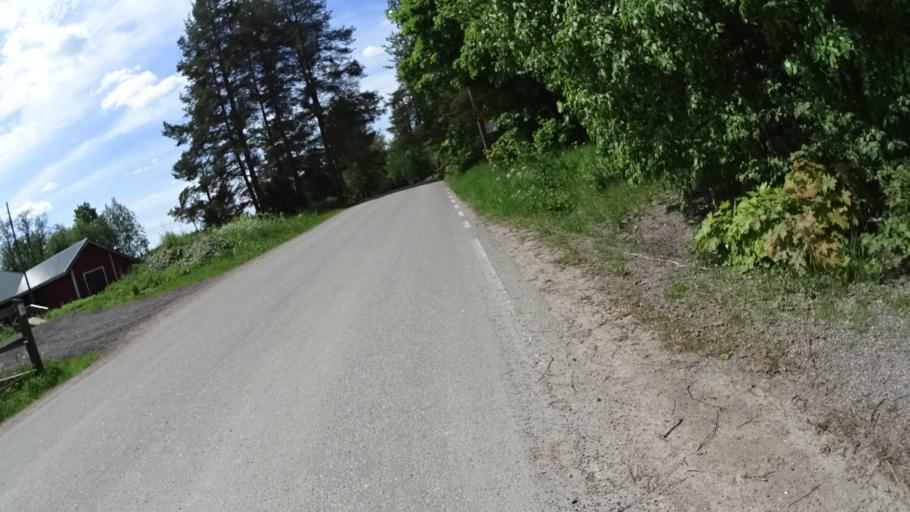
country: FI
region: Uusimaa
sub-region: Helsinki
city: Kauniainen
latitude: 60.2951
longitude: 24.6859
